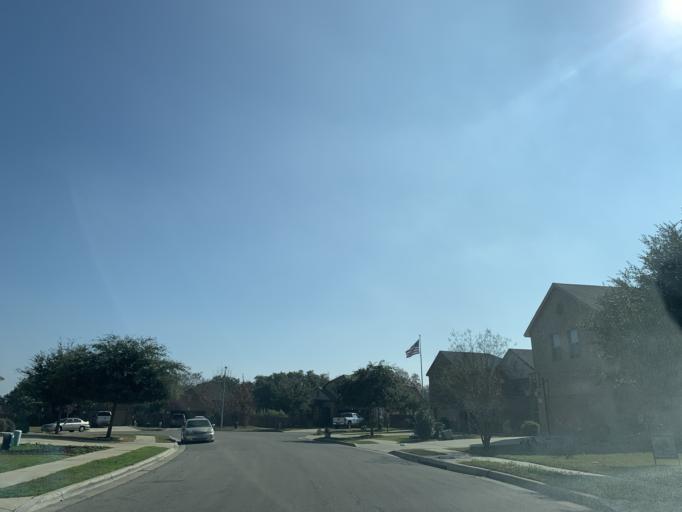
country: US
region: Texas
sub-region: Williamson County
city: Round Rock
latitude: 30.5298
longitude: -97.6409
